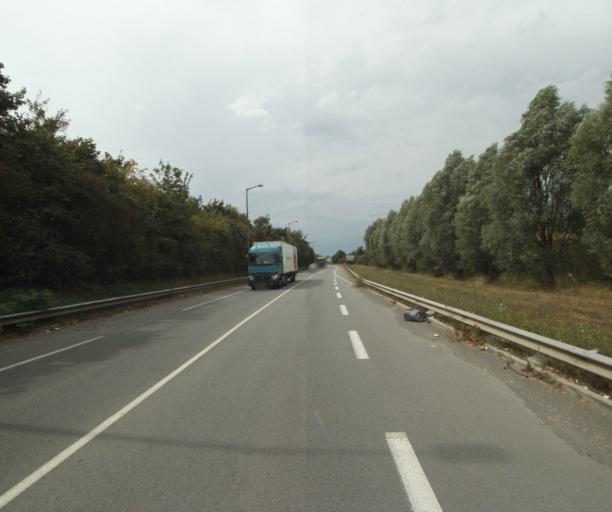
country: FR
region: Nord-Pas-de-Calais
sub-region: Departement du Nord
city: Wattrelos
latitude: 50.6883
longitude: 3.2166
